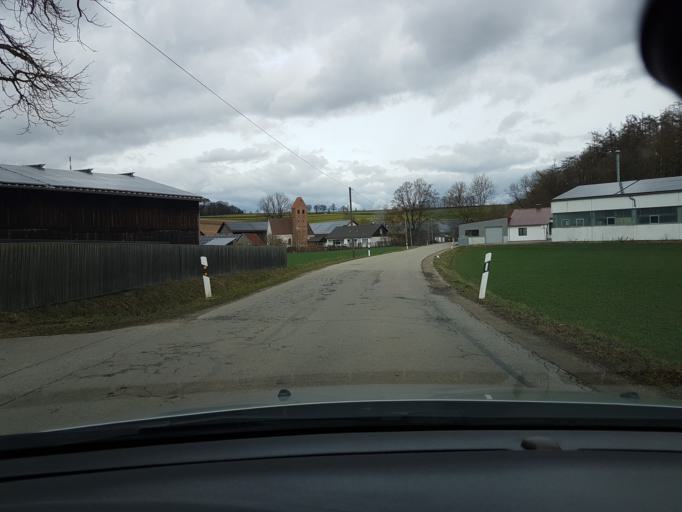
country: DE
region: Bavaria
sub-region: Lower Bavaria
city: Landshut
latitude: 48.5179
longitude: 12.1755
